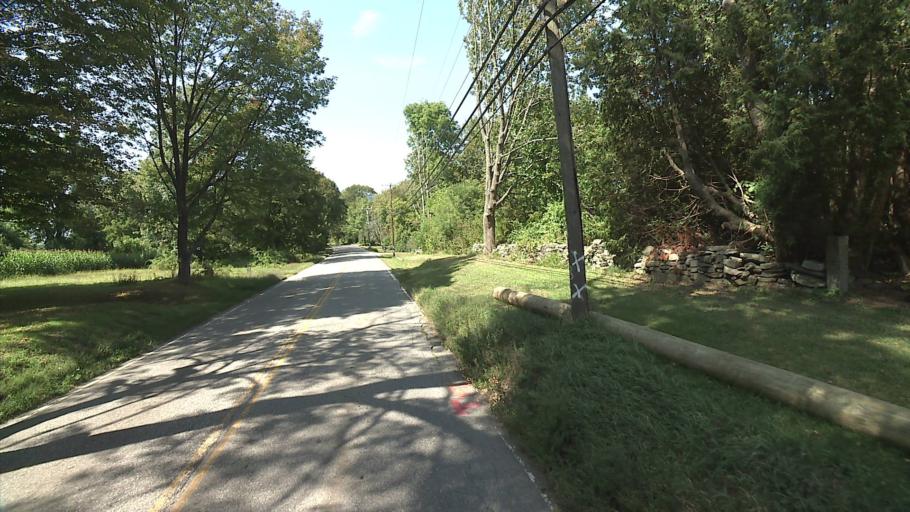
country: US
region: Connecticut
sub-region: Windham County
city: South Windham
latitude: 41.6293
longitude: -72.2013
